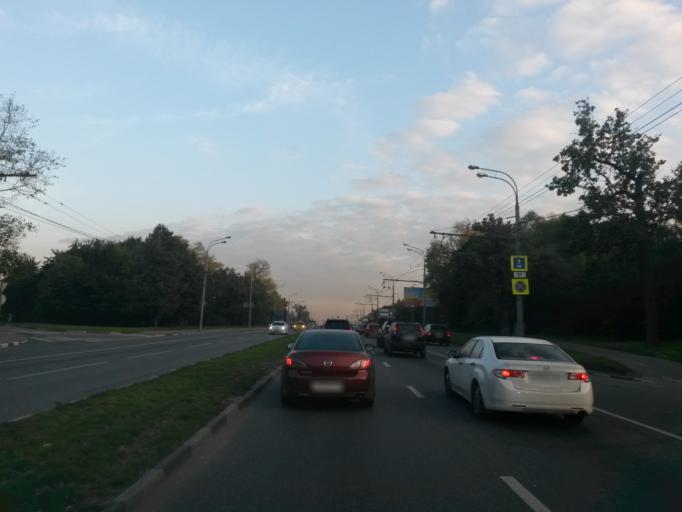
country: RU
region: Moscow
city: Tsaritsyno
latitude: 55.6119
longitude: 37.6626
